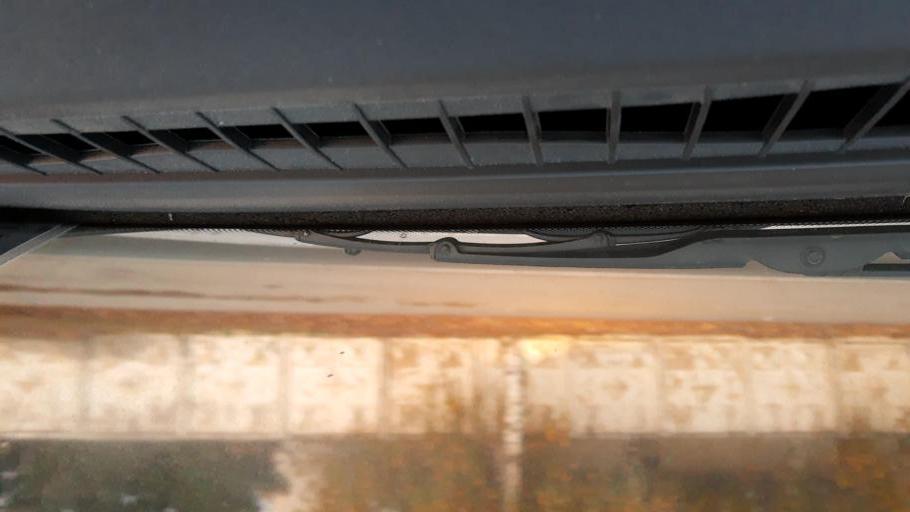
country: RU
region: Nizjnij Novgorod
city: Bor
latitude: 56.3802
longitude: 44.0365
